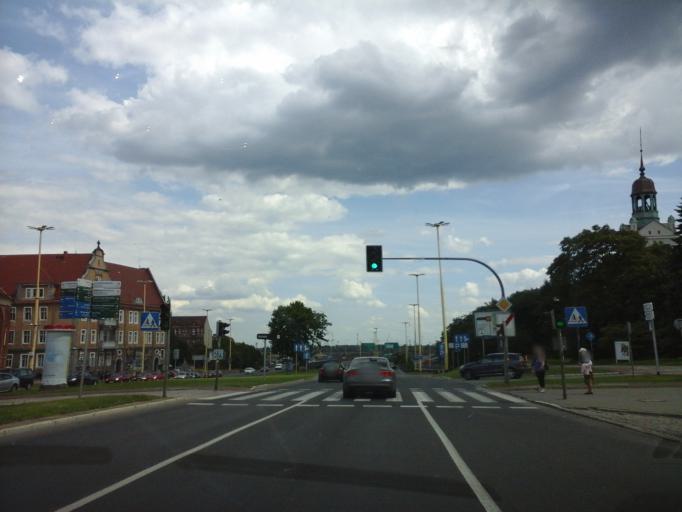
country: PL
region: West Pomeranian Voivodeship
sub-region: Szczecin
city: Szczecin
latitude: 53.4277
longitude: 14.5579
